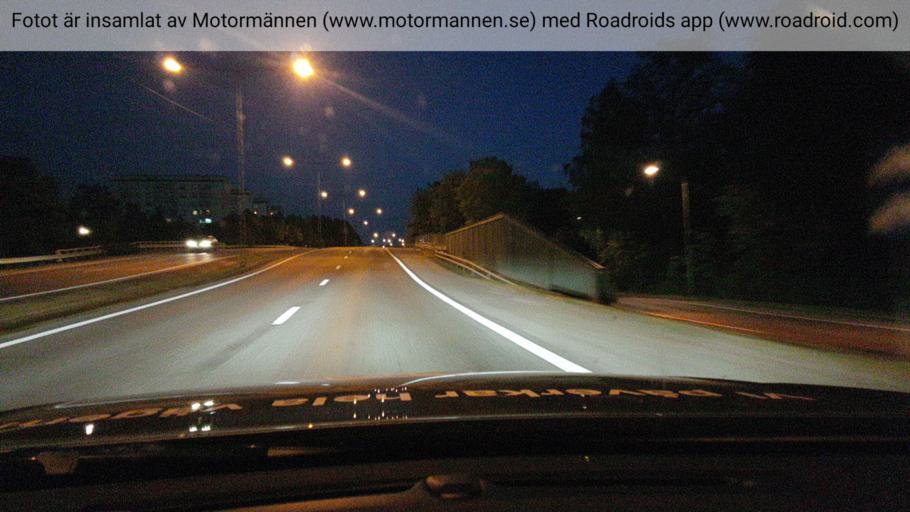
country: SE
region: Stockholm
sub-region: Huddinge Kommun
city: Huddinge
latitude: 59.2650
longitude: 18.0062
